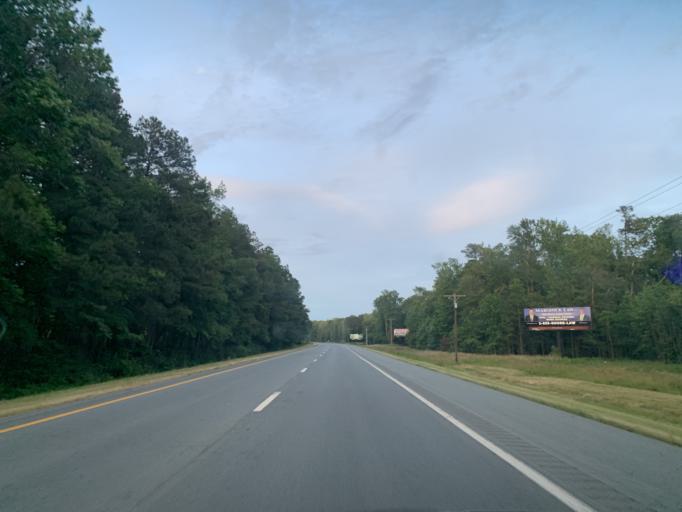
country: US
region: Maryland
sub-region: Wicomico County
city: Pittsville
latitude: 38.3847
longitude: -75.3403
